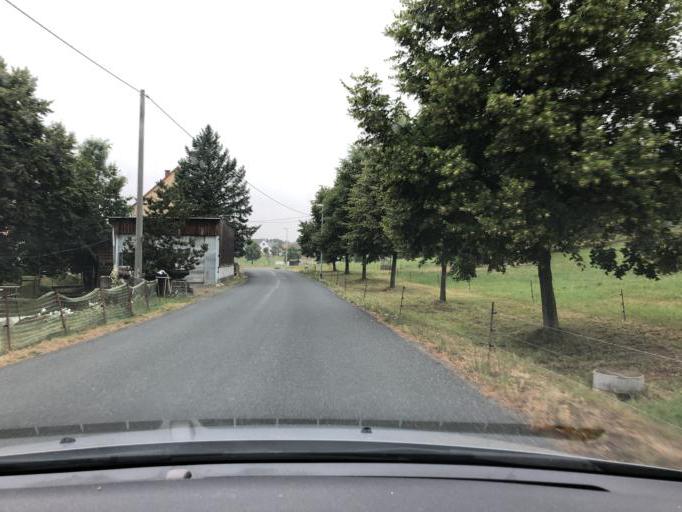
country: DE
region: Thuringia
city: Langenleuba-Niederhain
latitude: 50.9968
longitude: 12.6259
